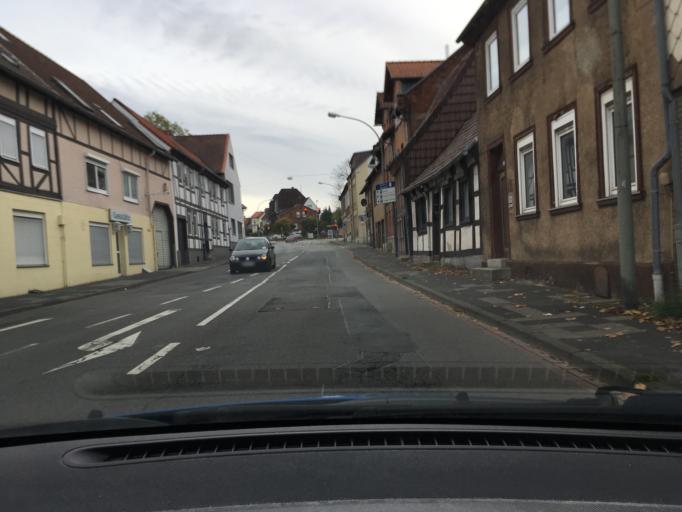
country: DE
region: Lower Saxony
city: Helmstedt
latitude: 52.2285
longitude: 11.0040
